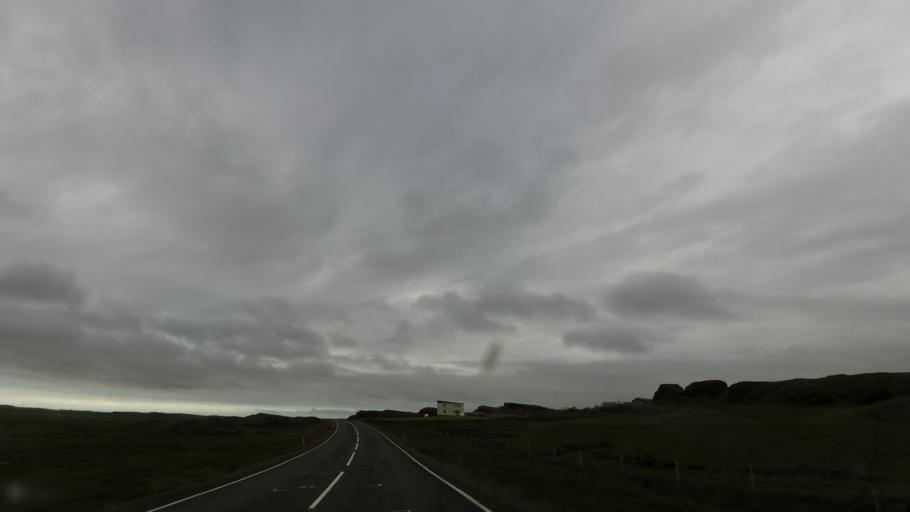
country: IS
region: East
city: Hoefn
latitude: 64.3312
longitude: -15.4138
